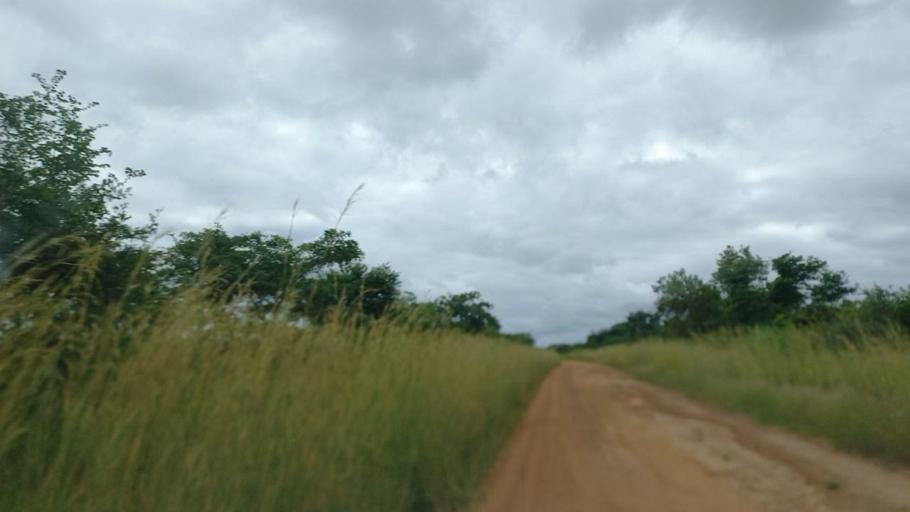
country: ZM
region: Lusaka
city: Chongwe
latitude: -15.4572
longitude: 28.8801
